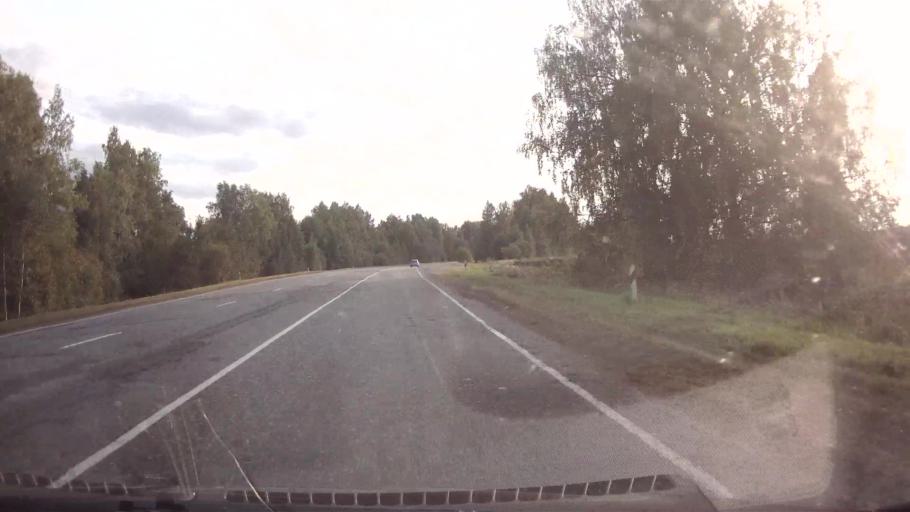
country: RU
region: Mariy-El
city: Sovetskiy
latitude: 56.7945
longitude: 48.6824
